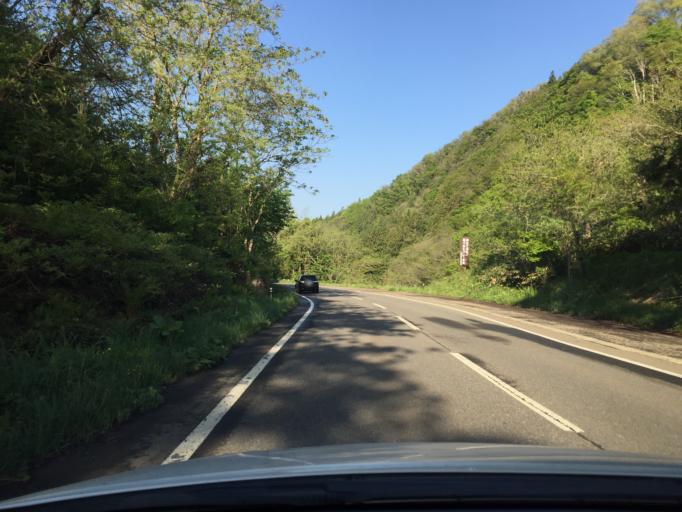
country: JP
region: Fukushima
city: Kitakata
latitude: 37.6647
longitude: 139.9650
